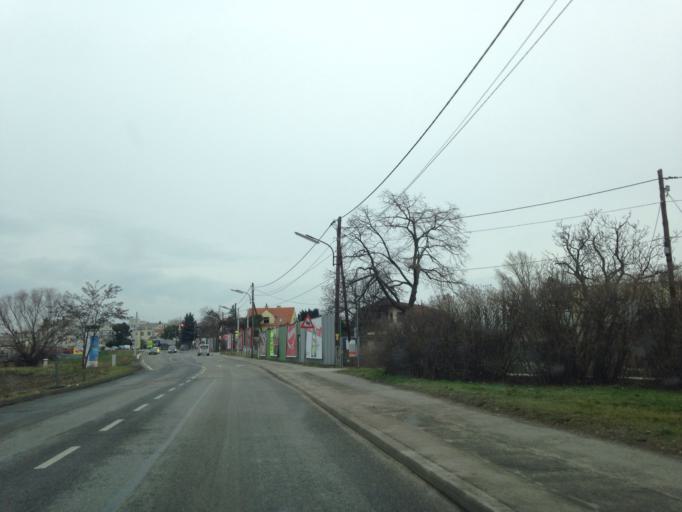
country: AT
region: Lower Austria
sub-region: Politischer Bezirk Wien-Umgebung
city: Gerasdorf bei Wien
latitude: 48.2641
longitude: 16.4350
